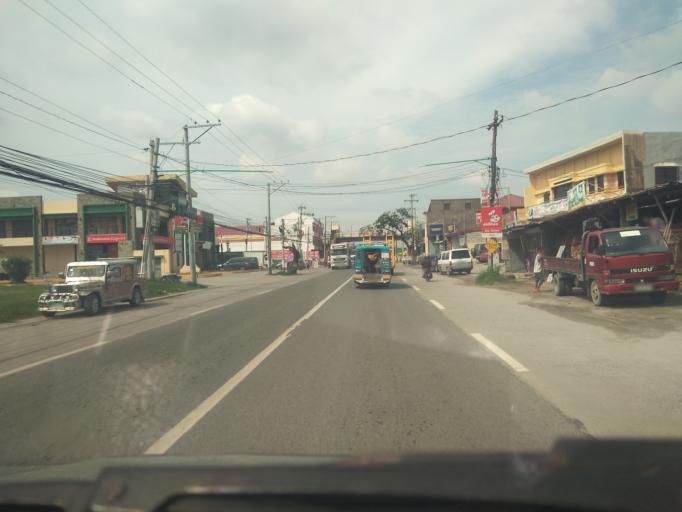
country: PH
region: Central Luzon
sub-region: Province of Pampanga
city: Pau
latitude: 15.0075
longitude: 120.7130
